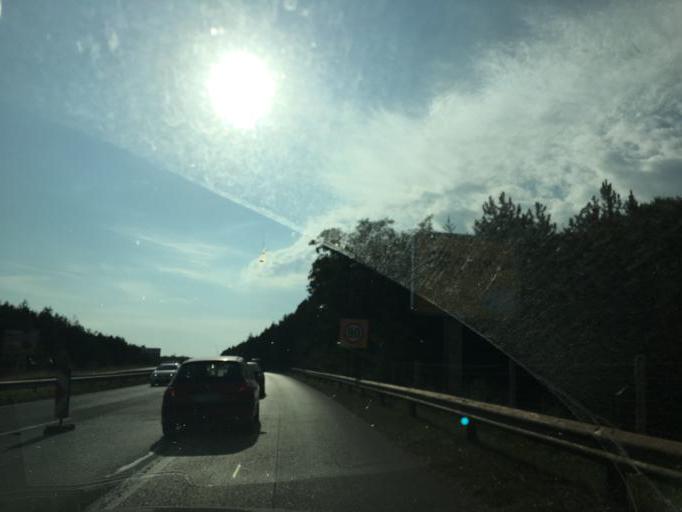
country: BG
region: Sofiya
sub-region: Obshtina Elin Pelin
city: Elin Pelin
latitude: 42.5892
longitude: 23.6254
